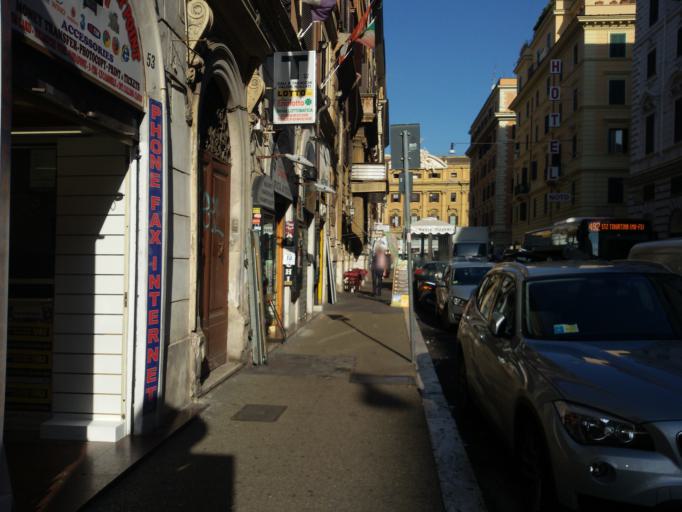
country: IT
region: Latium
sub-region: Citta metropolitana di Roma Capitale
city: Rome
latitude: 41.9041
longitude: 12.5001
